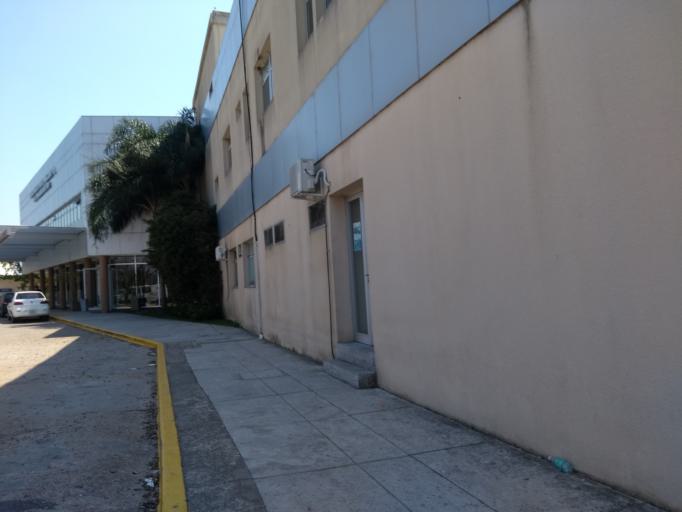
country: AR
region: Corrientes
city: Corrientes
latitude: -27.4492
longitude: -58.7581
